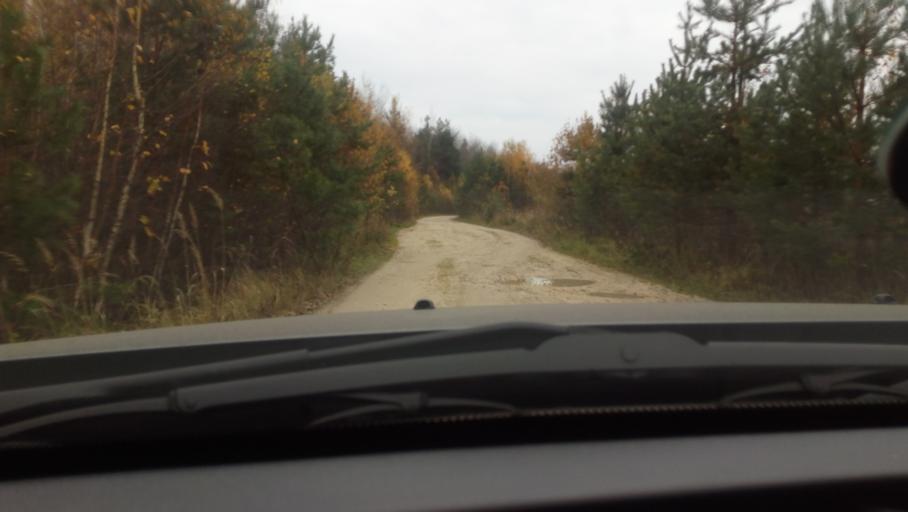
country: RU
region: Moskovskaya
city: Avsyunino
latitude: 55.5851
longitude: 39.2631
